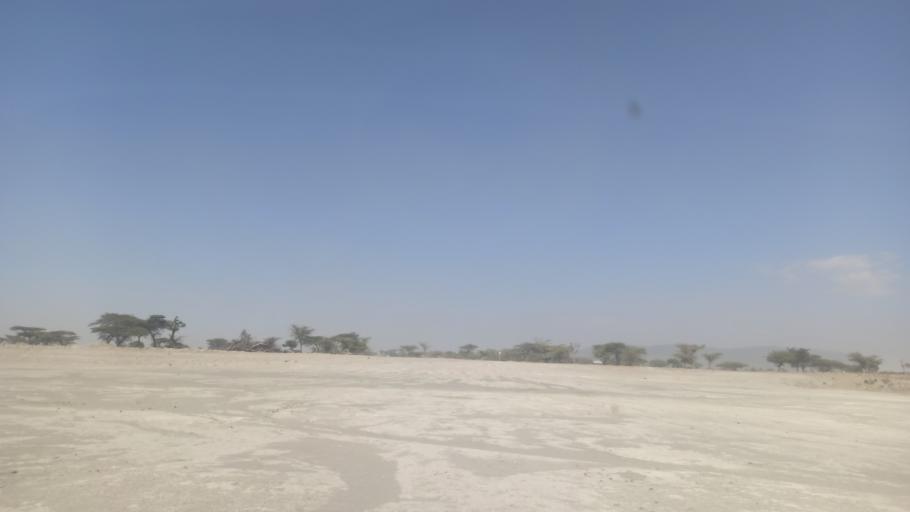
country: ET
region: Oromiya
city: Ziway
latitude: 7.6881
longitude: 38.6552
